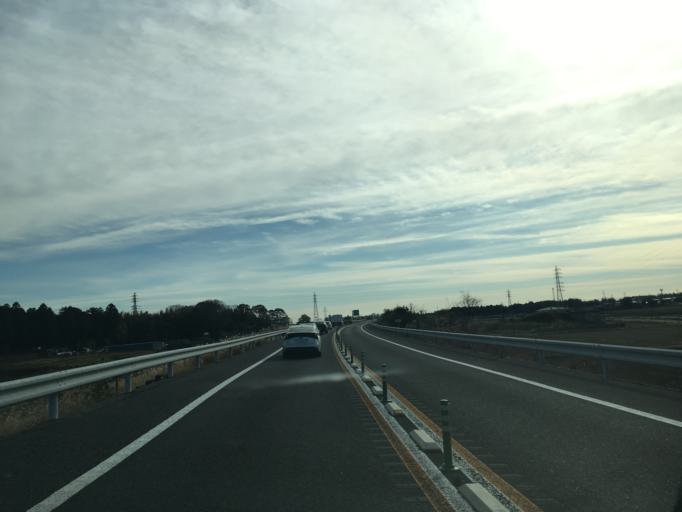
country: JP
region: Ibaraki
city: Naka
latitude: 36.0501
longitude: 140.1049
